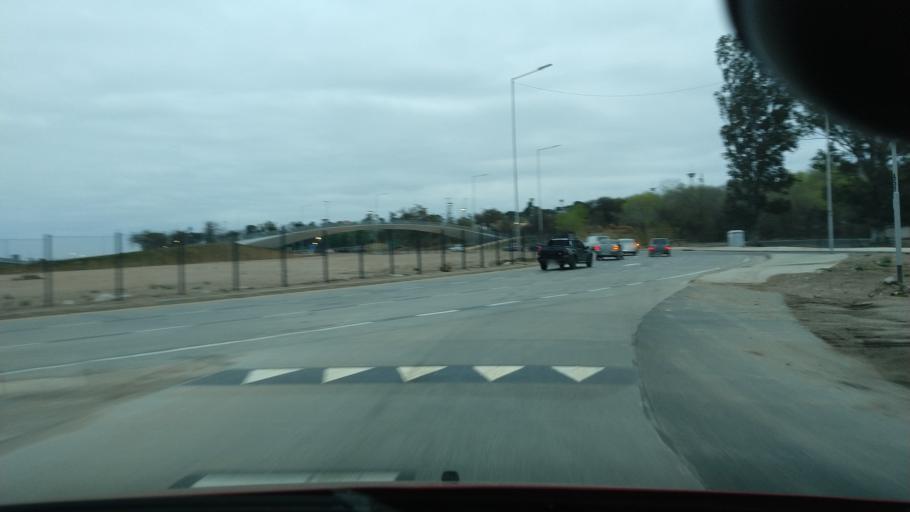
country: AR
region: Cordoba
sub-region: Departamento de Capital
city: Cordoba
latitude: -31.3690
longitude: -64.2513
